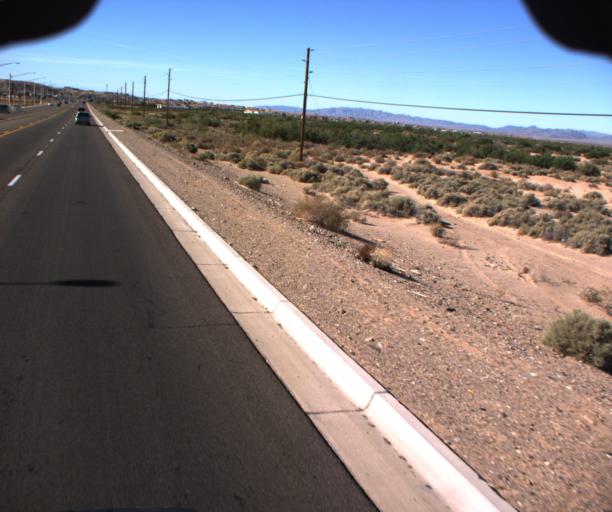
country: US
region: Arizona
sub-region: Mohave County
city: Bullhead City
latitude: 35.0660
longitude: -114.5893
